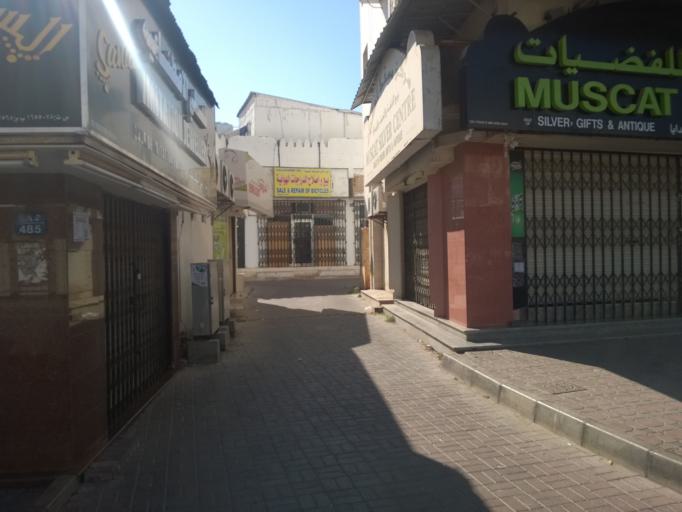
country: OM
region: Muhafazat Masqat
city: As Sib al Jadidah
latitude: 23.6780
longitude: 58.1892
